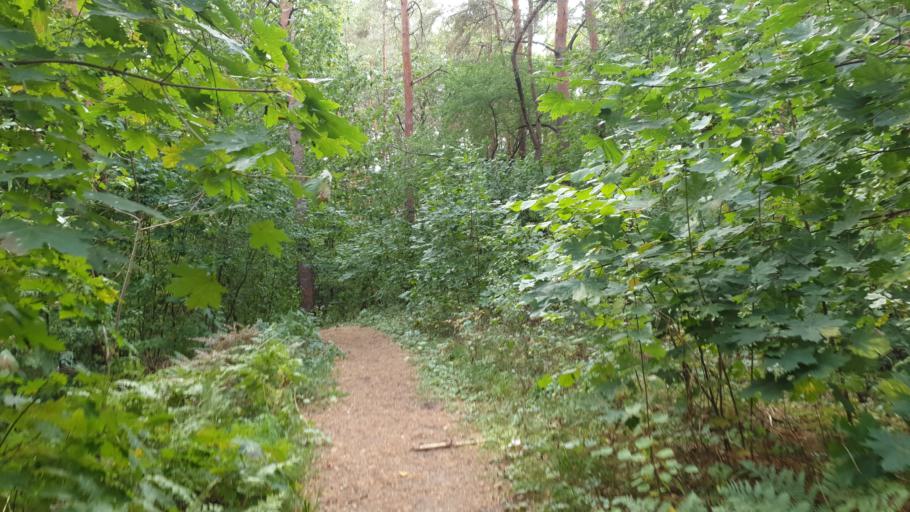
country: LT
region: Vilnius County
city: Seskine
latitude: 54.6971
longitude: 25.2348
